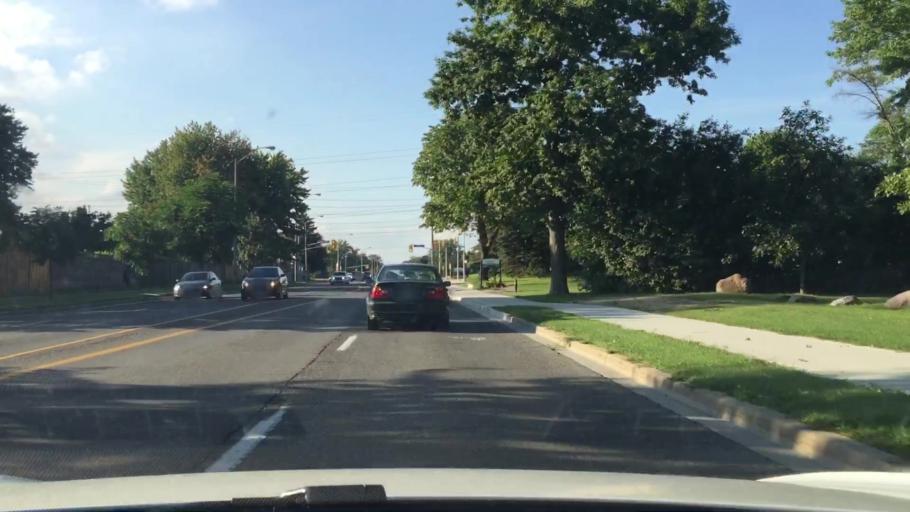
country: CA
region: Ontario
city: Scarborough
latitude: 43.8058
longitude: -79.3098
